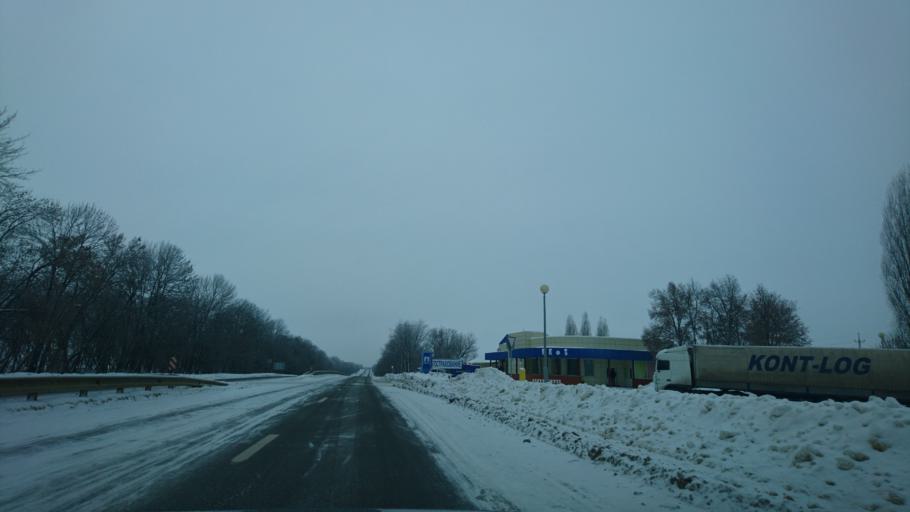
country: RU
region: Belgorod
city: Mayskiy
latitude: 50.4349
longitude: 36.3891
